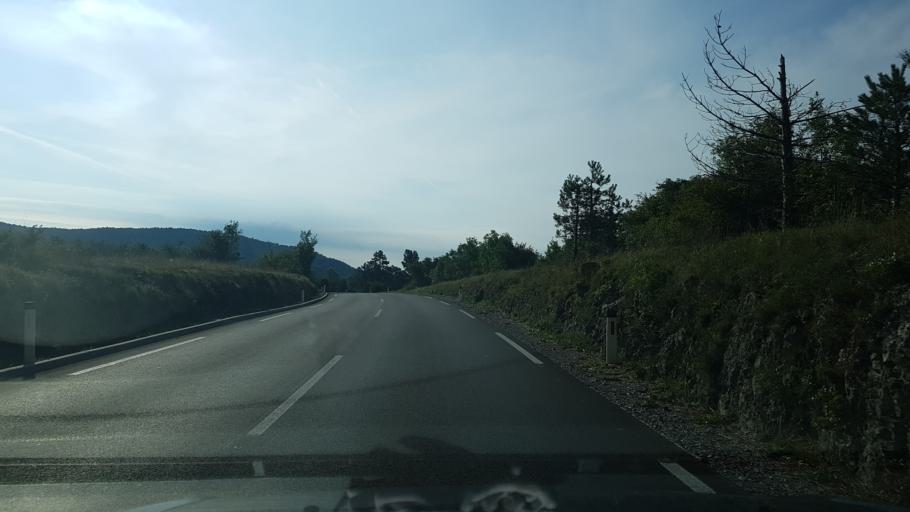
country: SI
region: Divaca
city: Divaca
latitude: 45.6745
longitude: 14.0100
